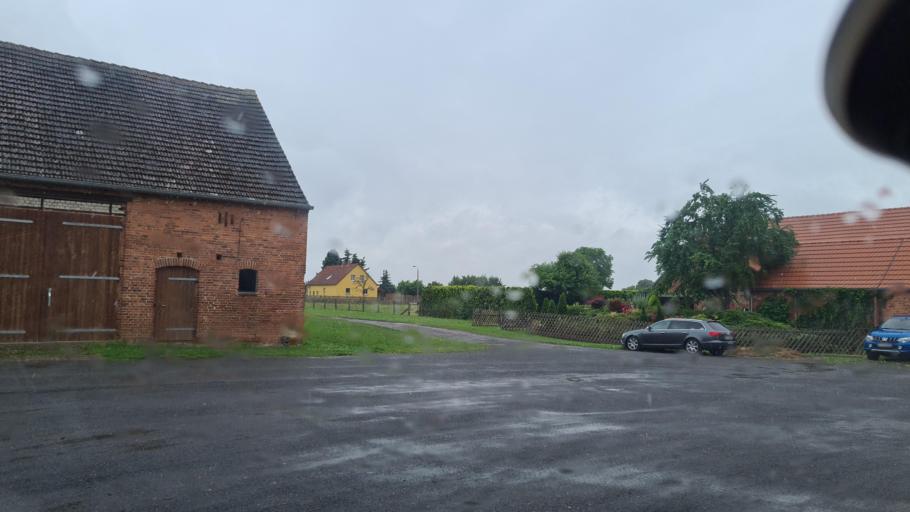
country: DE
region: Brandenburg
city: Juterbog
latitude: 51.9831
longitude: 13.1729
